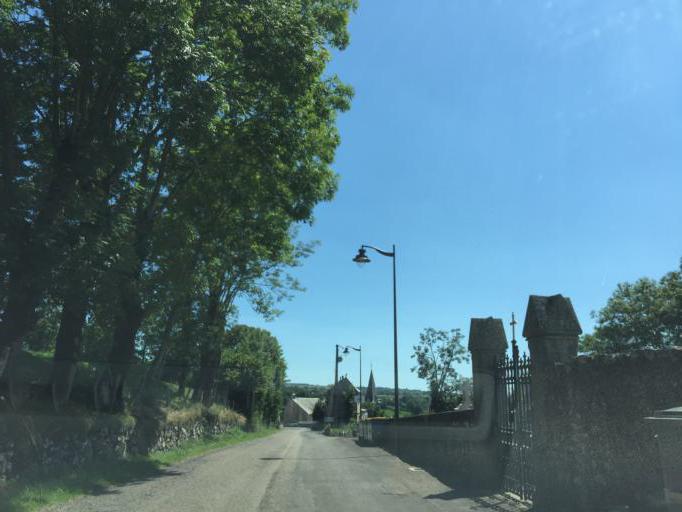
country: FR
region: Midi-Pyrenees
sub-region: Departement de l'Aveyron
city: Laguiole
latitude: 44.6543
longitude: 2.8645
